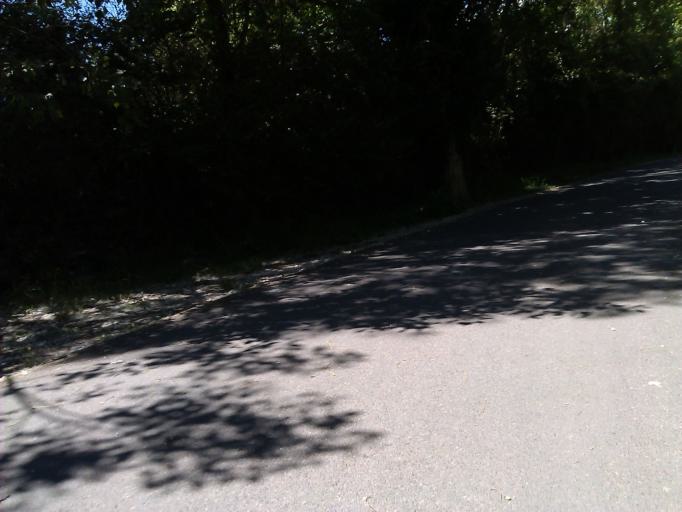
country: ES
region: Castille and Leon
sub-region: Provincia de Leon
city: Leon
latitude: 42.5936
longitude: -5.5501
